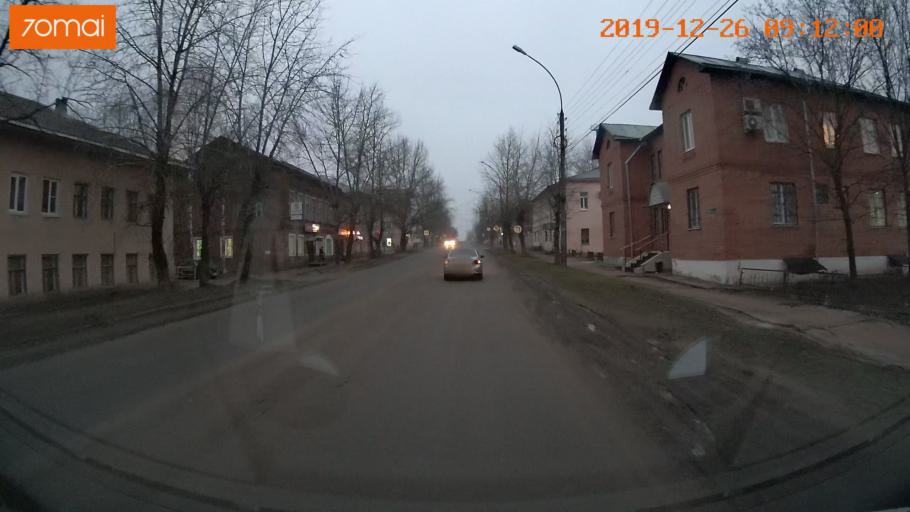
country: RU
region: Vologda
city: Gryazovets
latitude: 58.8788
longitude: 40.2531
